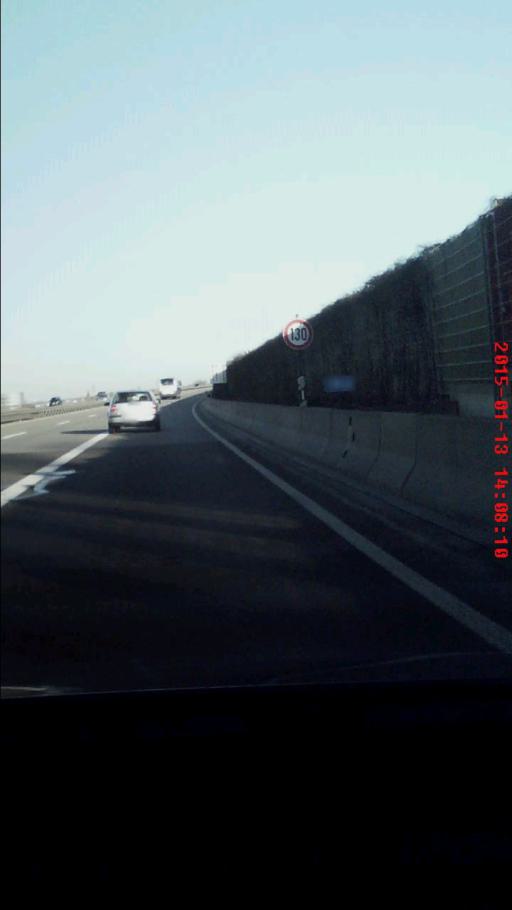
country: DE
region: Thuringia
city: Elxleben
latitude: 51.0258
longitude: 10.9779
